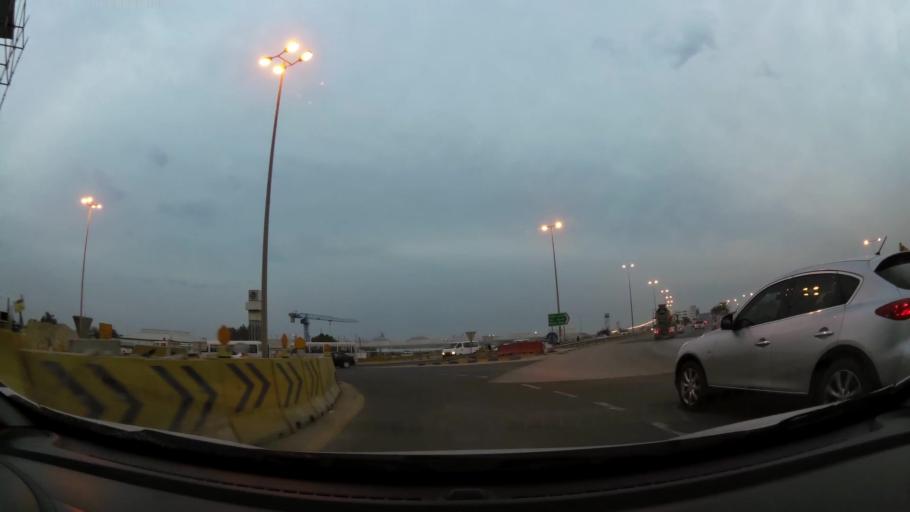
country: BH
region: Northern
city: Ar Rifa'
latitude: 26.1224
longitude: 50.5914
